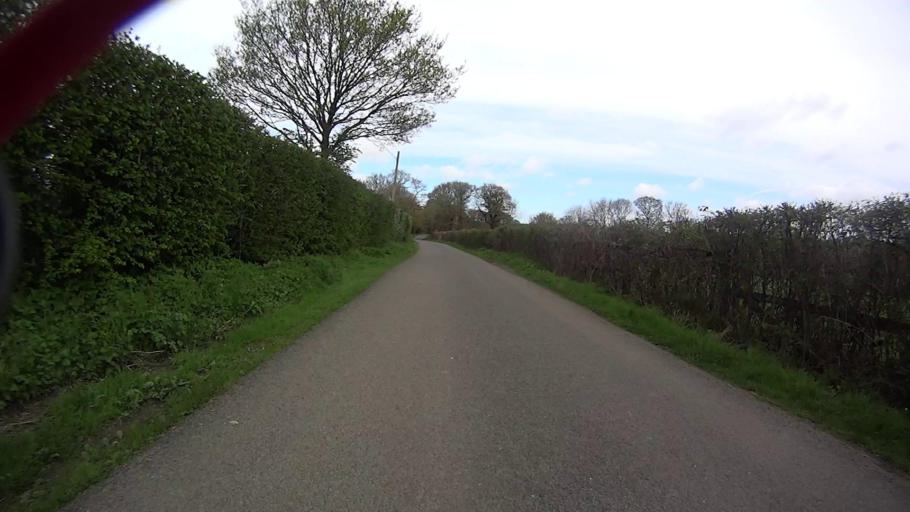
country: GB
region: England
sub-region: West Sussex
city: Bewbush
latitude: 51.1307
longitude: -0.2572
